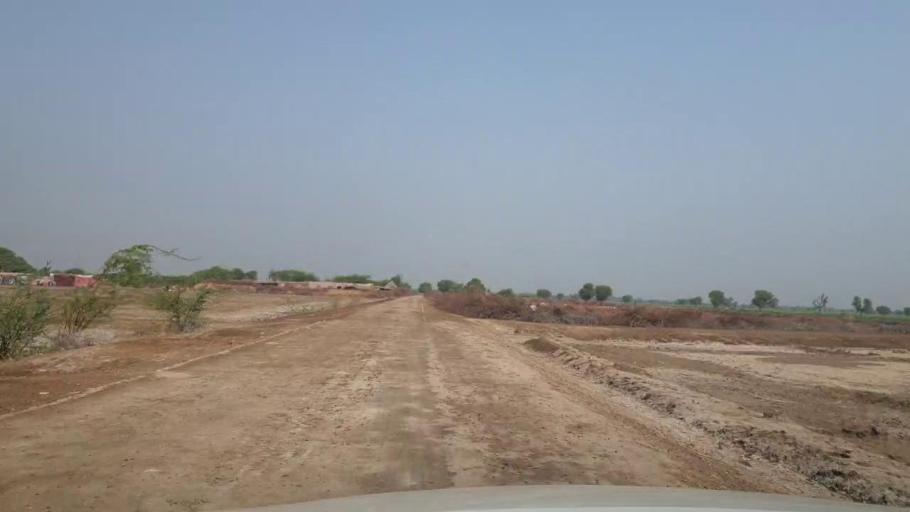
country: PK
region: Sindh
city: Umarkot
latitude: 25.4301
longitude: 69.7061
